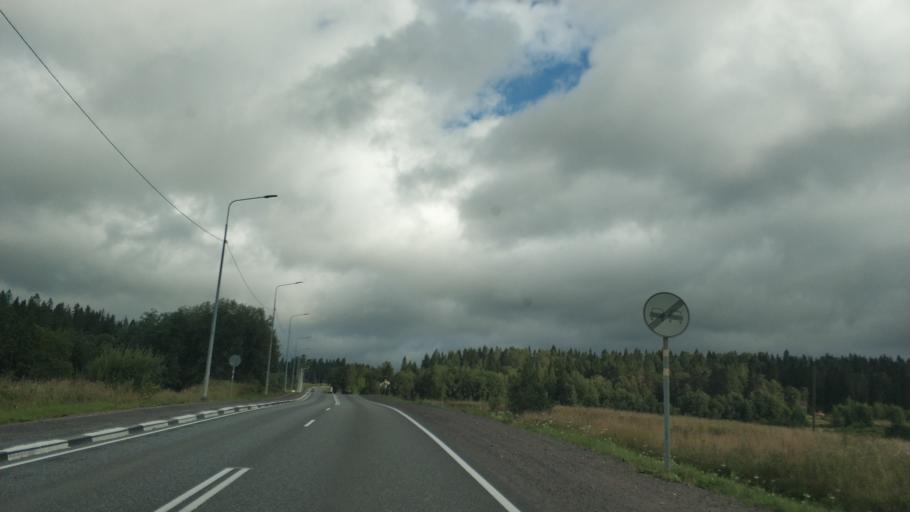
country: RU
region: Republic of Karelia
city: Khelyulya
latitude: 61.7632
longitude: 30.6562
